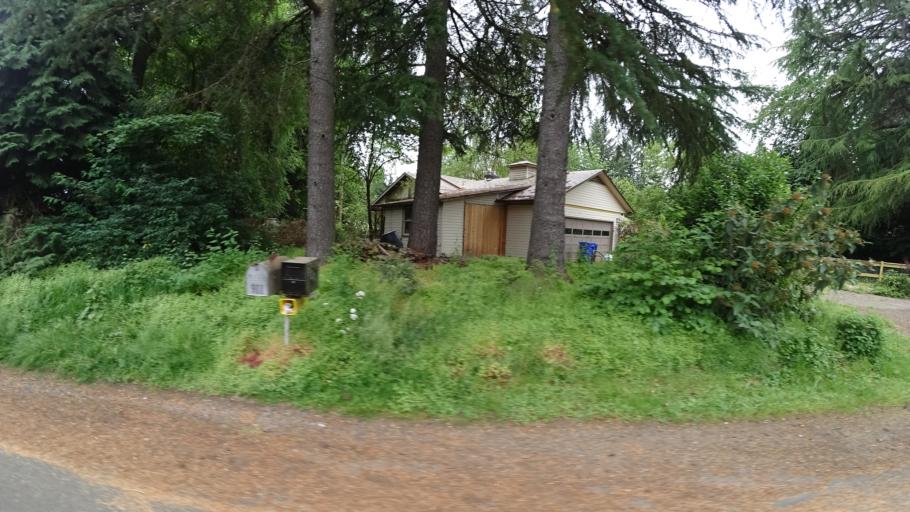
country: US
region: Oregon
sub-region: Clackamas County
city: Lake Oswego
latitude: 45.4413
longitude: -122.6877
